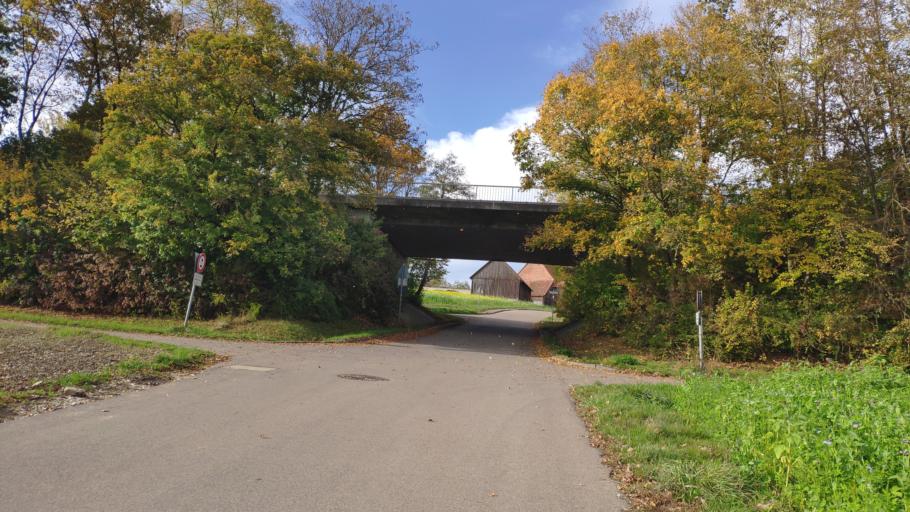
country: DE
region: Baden-Wuerttemberg
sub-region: Tuebingen Region
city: Erbach
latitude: 48.3881
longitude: 9.9137
